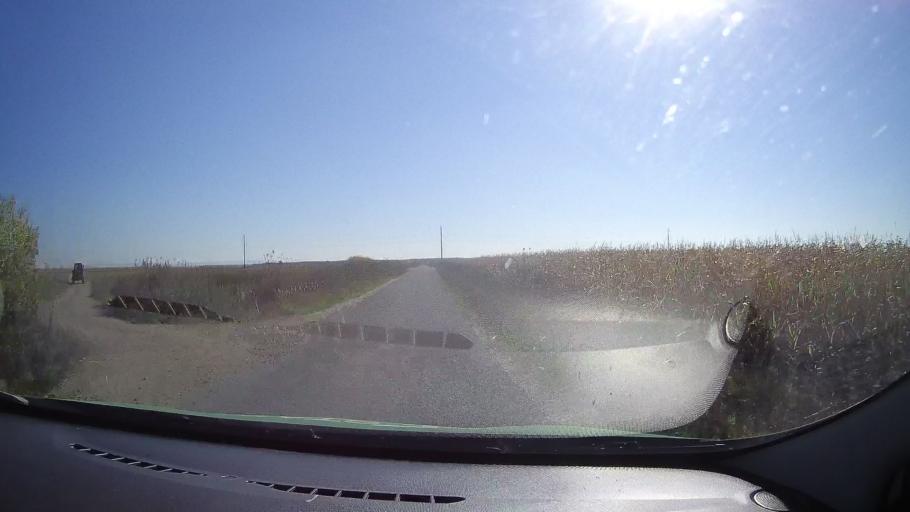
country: RO
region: Satu Mare
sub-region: Comuna Doba
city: Doba
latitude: 47.7375
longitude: 22.7194
